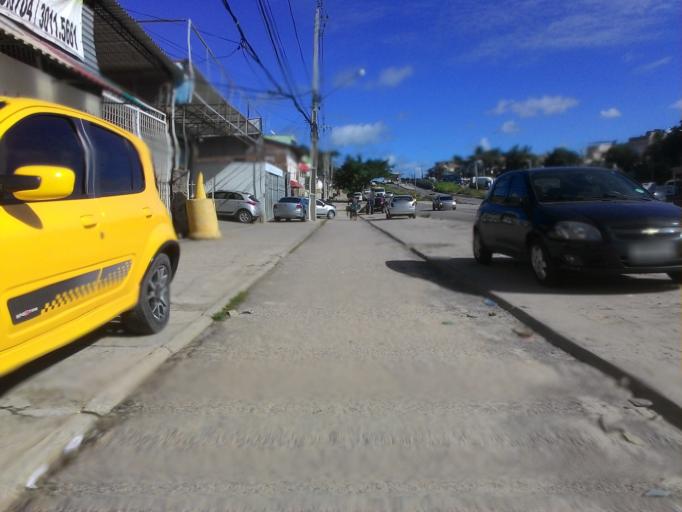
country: BR
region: Pernambuco
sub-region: Olinda
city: Olinda
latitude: -7.9920
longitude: -34.8548
